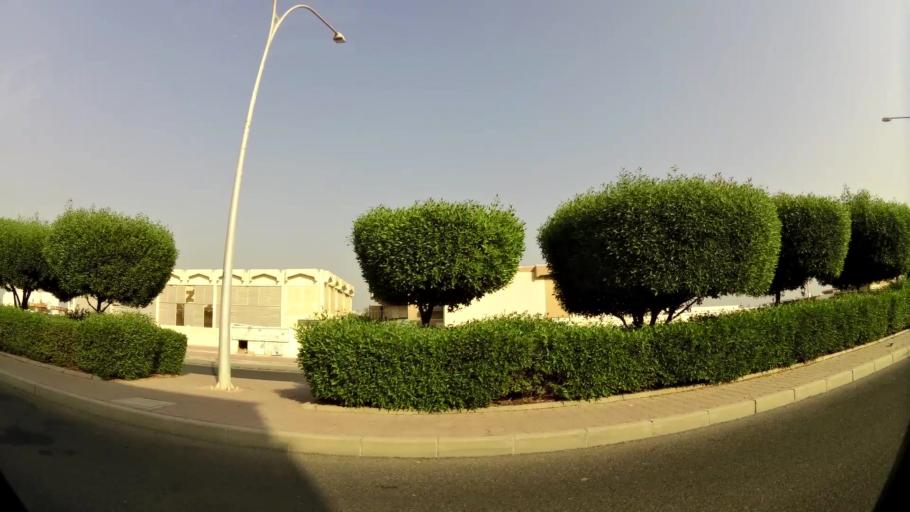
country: KW
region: Al Ahmadi
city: Ar Riqqah
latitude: 29.1146
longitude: 48.1054
